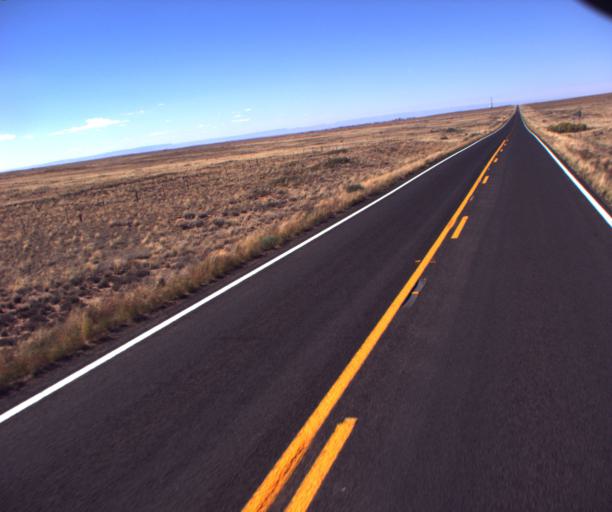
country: US
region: Arizona
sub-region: Coconino County
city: Tuba City
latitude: 35.9813
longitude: -110.9893
